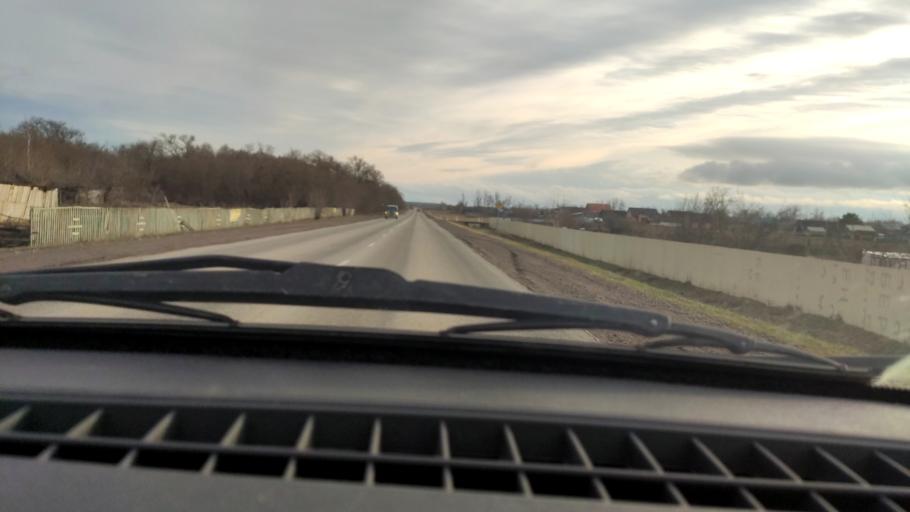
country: RU
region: Bashkortostan
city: Davlekanovo
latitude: 54.2937
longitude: 55.1240
